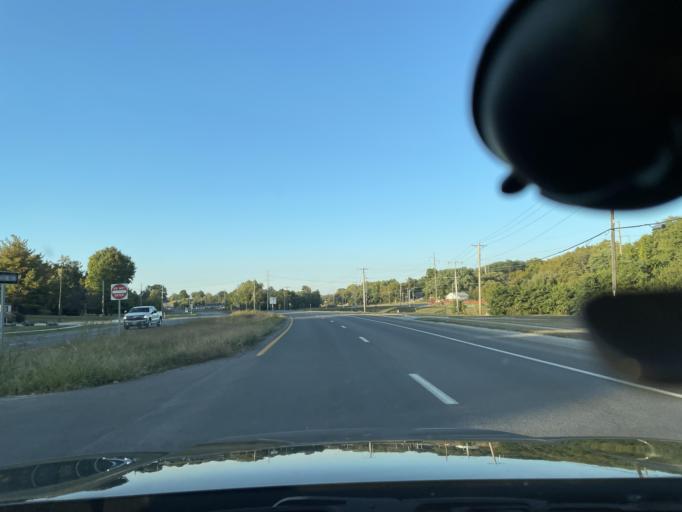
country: US
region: Missouri
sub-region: Andrew County
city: Country Club Village
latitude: 39.8042
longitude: -94.8417
